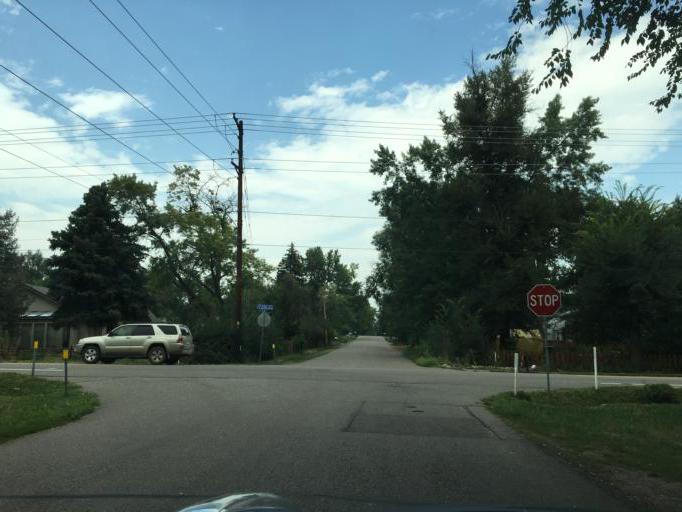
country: US
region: Colorado
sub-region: Jefferson County
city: Wheat Ridge
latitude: 39.7473
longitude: -105.0931
